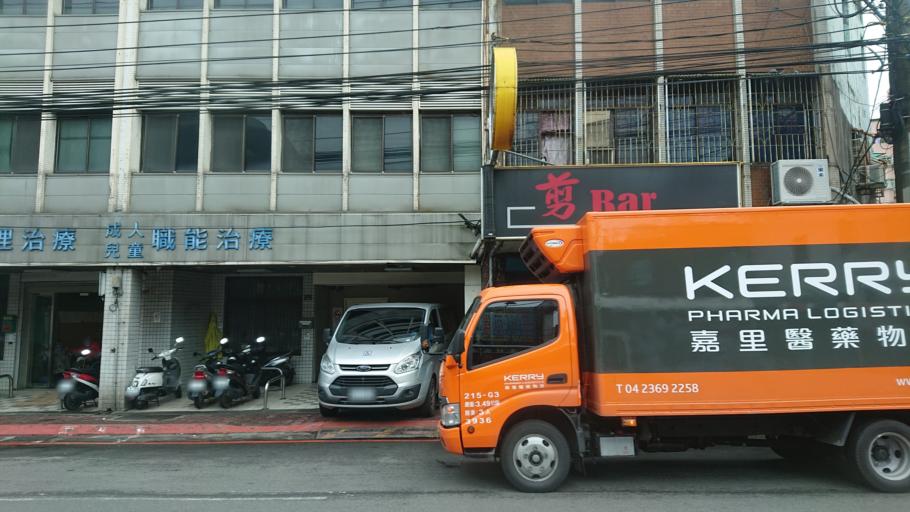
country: TW
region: Taipei
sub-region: Taipei
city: Banqiao
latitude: 24.9714
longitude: 121.4400
